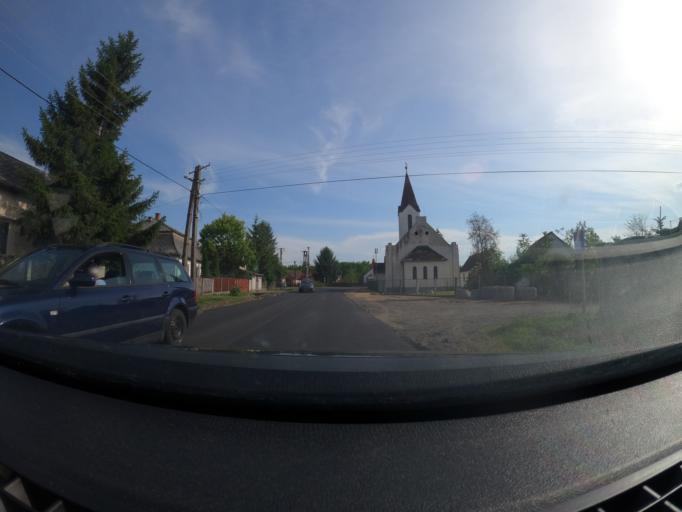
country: HU
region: Hajdu-Bihar
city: Nyirabrany
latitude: 47.5318
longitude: 21.9983
